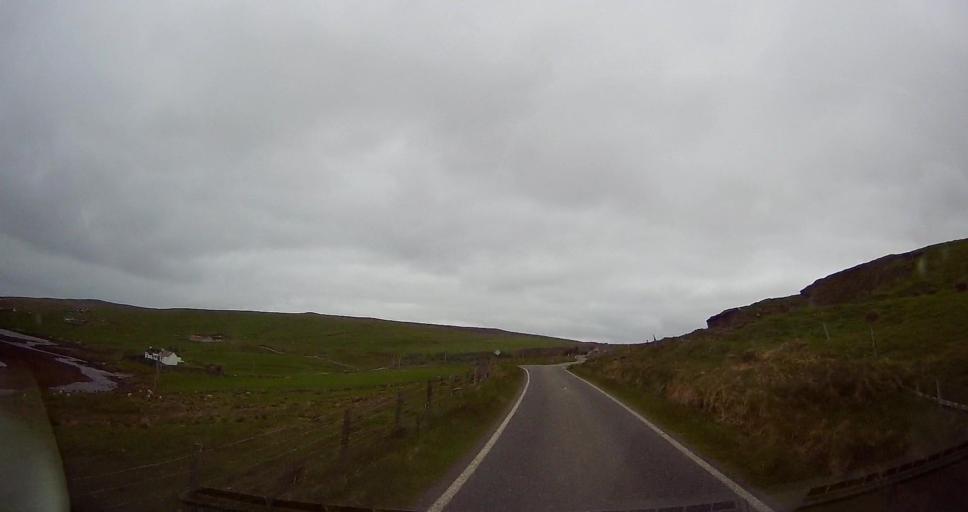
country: GB
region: Scotland
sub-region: Shetland Islands
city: Lerwick
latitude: 60.3021
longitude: -1.3368
